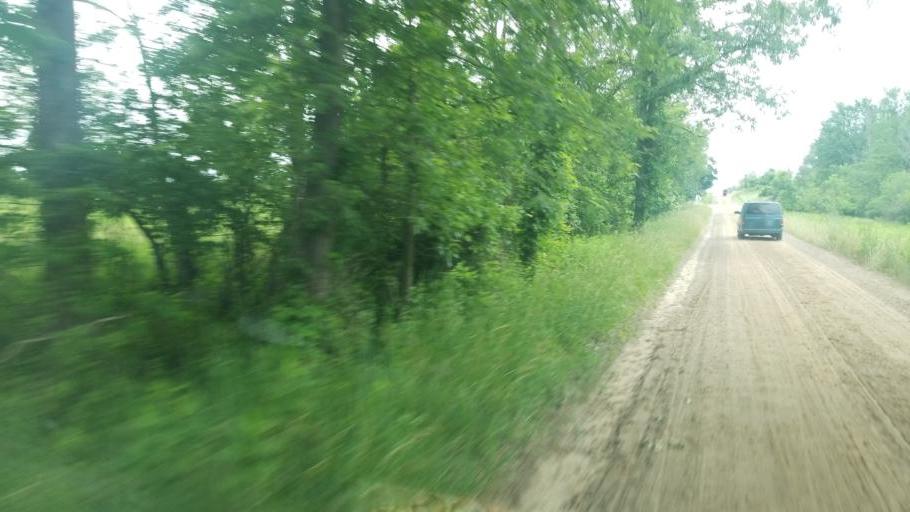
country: US
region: Michigan
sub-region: Barry County
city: Nashville
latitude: 42.6537
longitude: -84.9755
